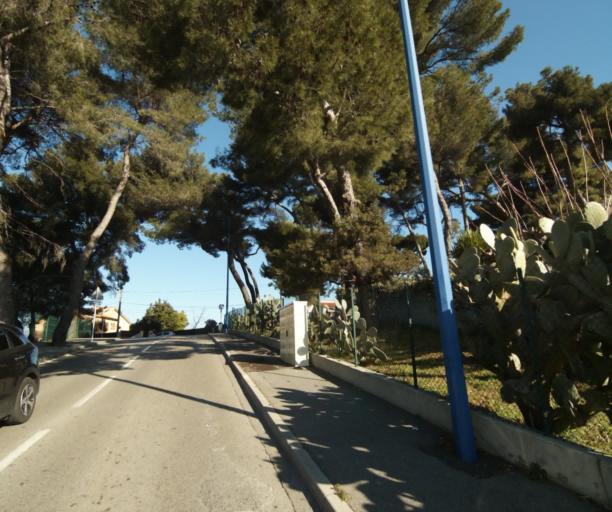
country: FR
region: Provence-Alpes-Cote d'Azur
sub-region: Departement des Alpes-Maritimes
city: Biot
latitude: 43.6040
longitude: 7.0921
